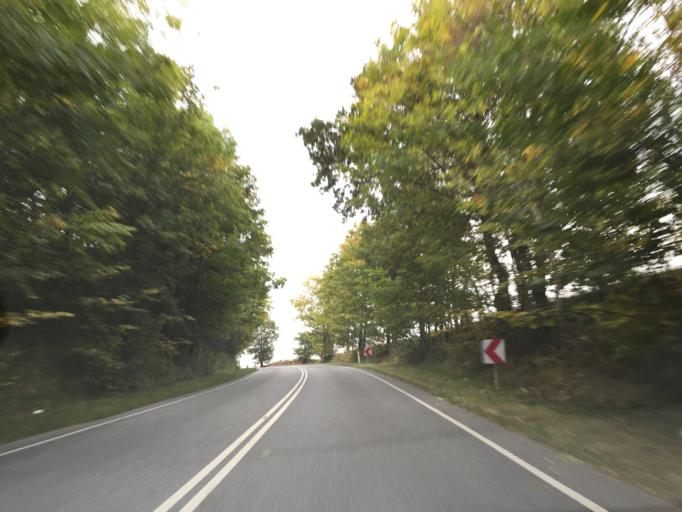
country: DK
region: Central Jutland
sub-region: Viborg Kommune
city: Bjerringbro
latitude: 56.3158
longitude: 9.6876
